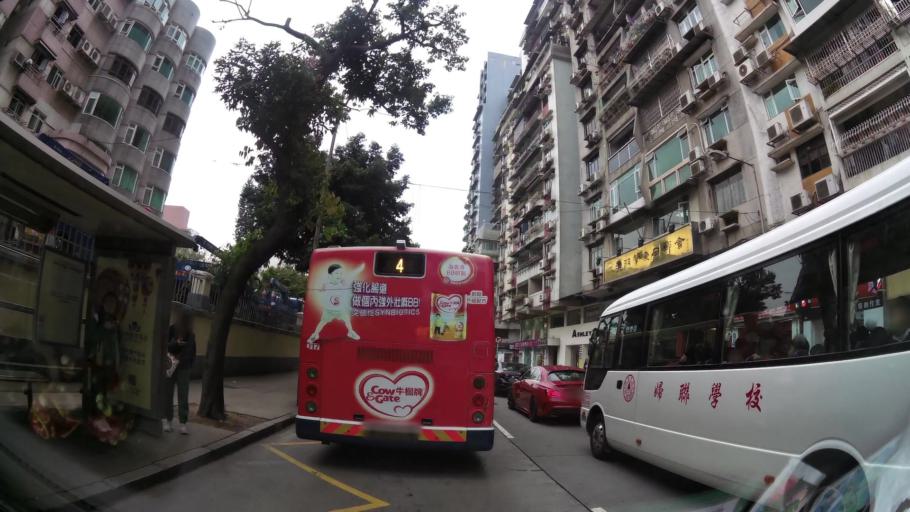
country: MO
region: Macau
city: Macau
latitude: 22.1993
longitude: 113.5488
